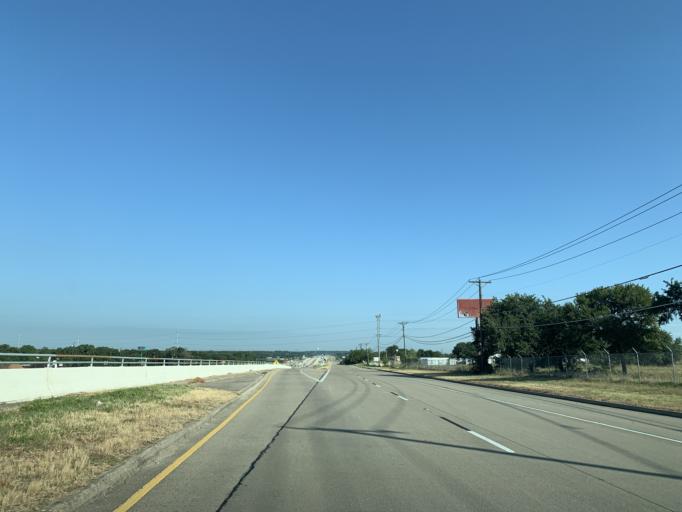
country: US
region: Texas
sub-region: Tarrant County
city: Lakeside
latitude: 32.8281
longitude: -97.4808
